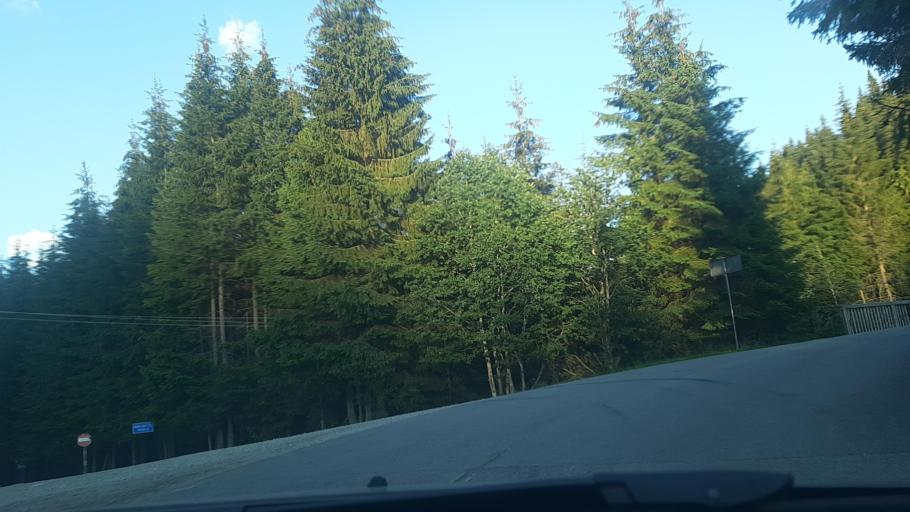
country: RO
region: Gorj
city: Novaci-Straini
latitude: 45.4320
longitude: 23.6677
